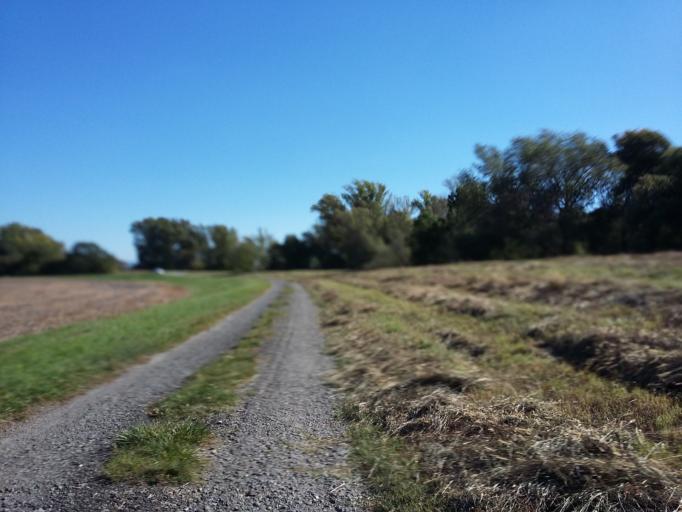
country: AT
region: Lower Austria
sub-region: Politischer Bezirk Ganserndorf
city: Marchegg
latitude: 48.2986
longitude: 16.9237
